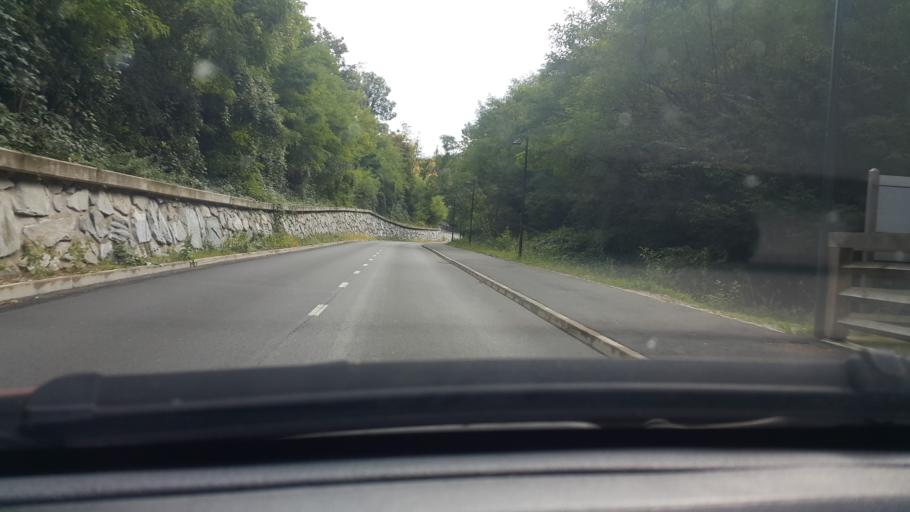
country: SI
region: Maribor
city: Maribor
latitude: 46.5686
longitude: 15.6445
